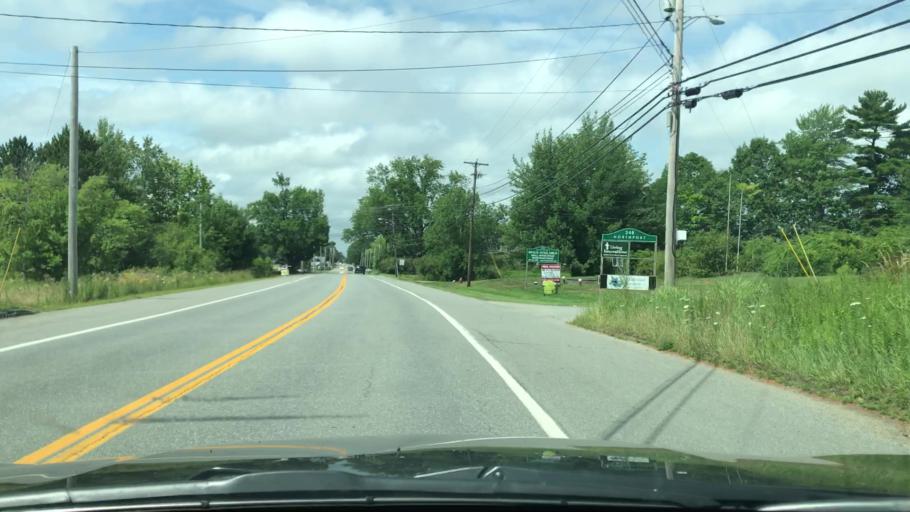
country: US
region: Maine
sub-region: Waldo County
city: Belfast
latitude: 44.3997
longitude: -68.9875
